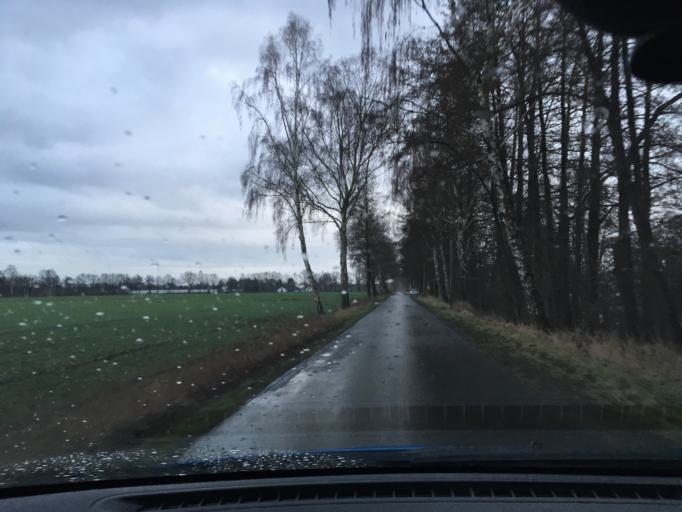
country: DE
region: Lower Saxony
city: Ludersburg
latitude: 53.3157
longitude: 10.6029
